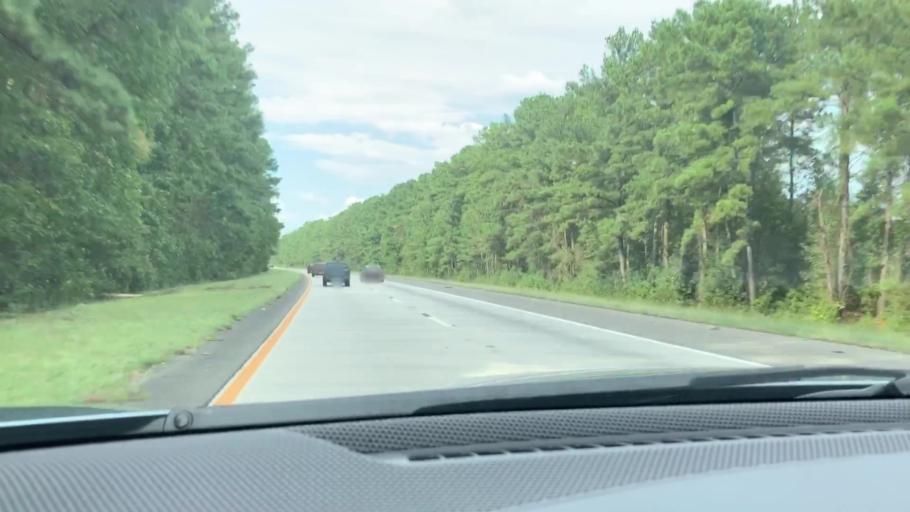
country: US
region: South Carolina
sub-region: Colleton County
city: Walterboro
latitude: 33.0219
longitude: -80.6654
